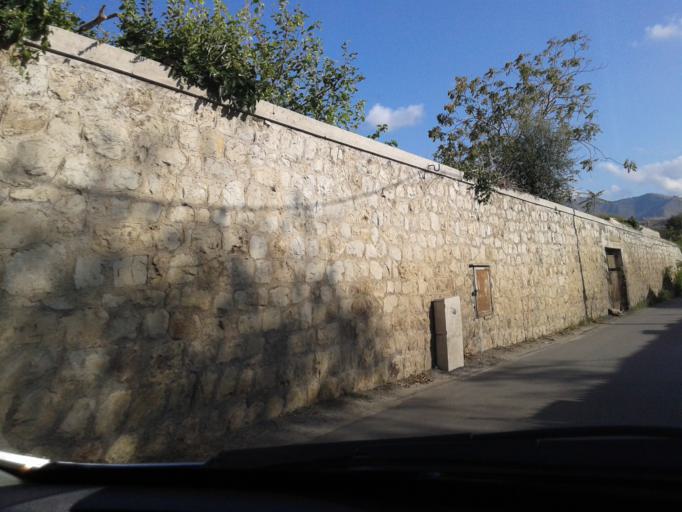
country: IT
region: Sicily
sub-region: Palermo
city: Monreale
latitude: 38.1023
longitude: 13.3158
